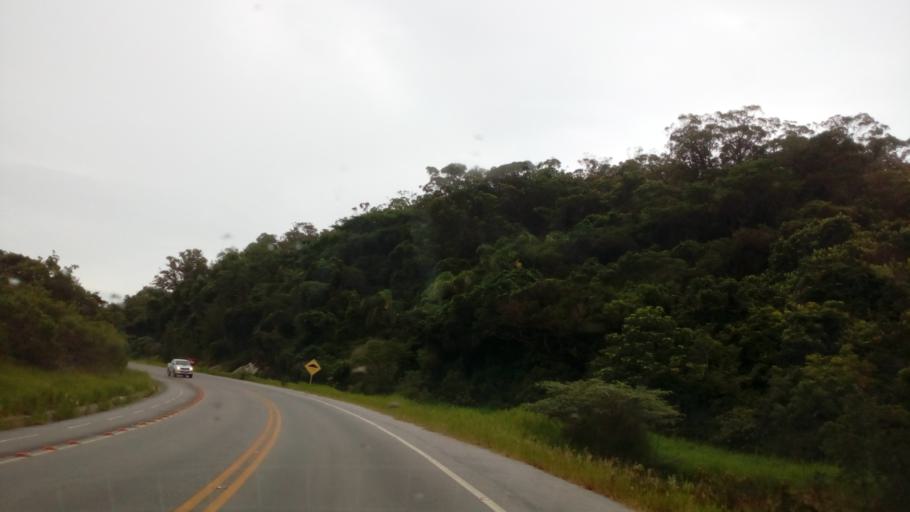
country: BR
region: Santa Catarina
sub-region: Laguna
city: Laguna
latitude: -28.5142
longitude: -48.7675
